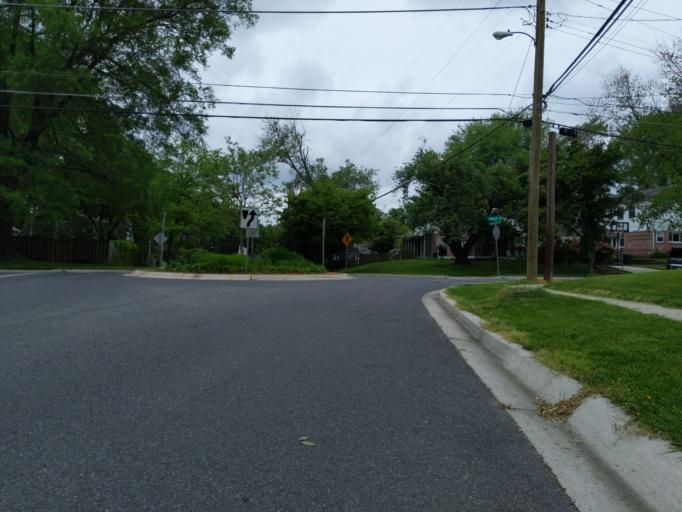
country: US
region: Maryland
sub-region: Montgomery County
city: Forest Glen
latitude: 39.0185
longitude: -77.0396
